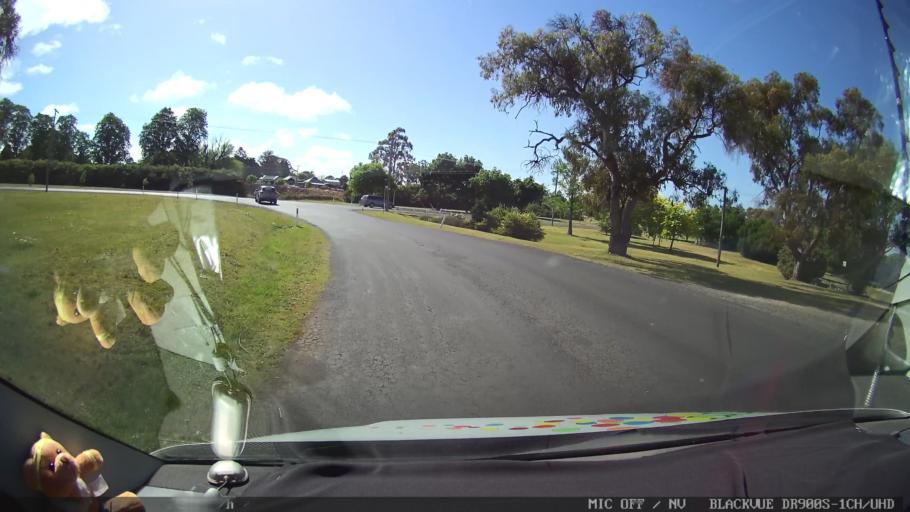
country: AU
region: New South Wales
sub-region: Guyra
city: Guyra
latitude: -30.2263
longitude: 151.6702
